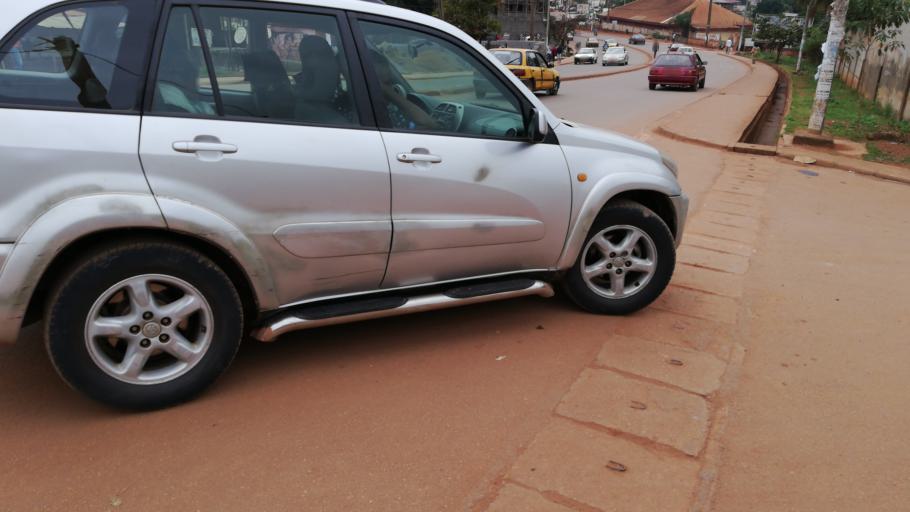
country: CM
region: Centre
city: Yaounde
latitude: 3.8687
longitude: 11.5580
